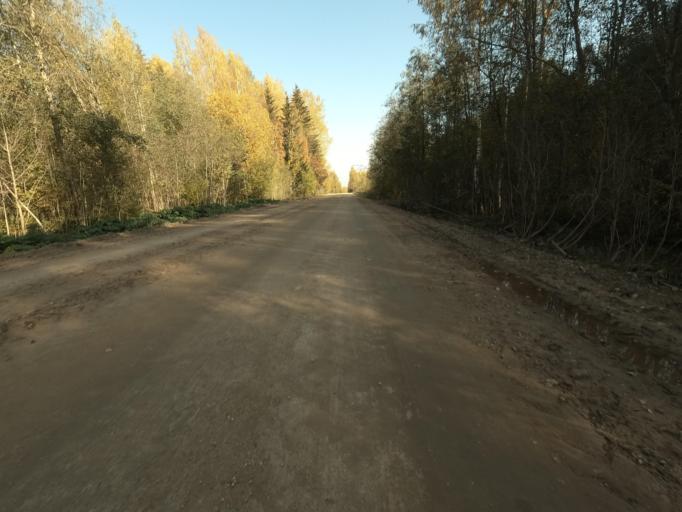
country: RU
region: Novgorod
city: Batetskiy
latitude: 58.8283
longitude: 30.7119
